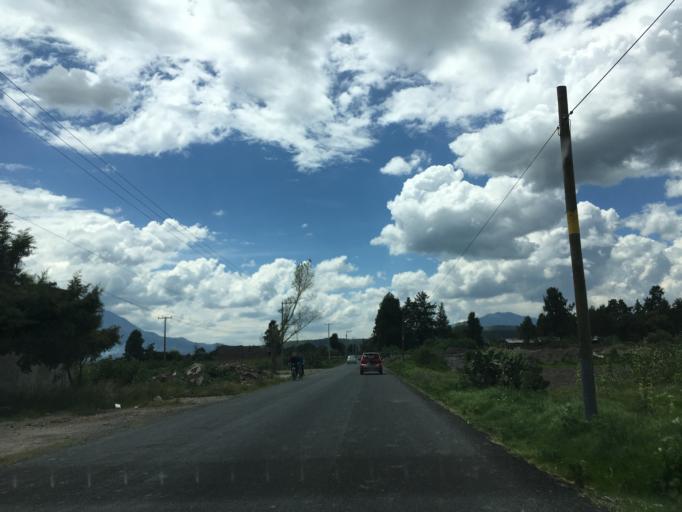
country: MX
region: Michoacan
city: Zacapu
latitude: 19.8400
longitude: -101.7537
